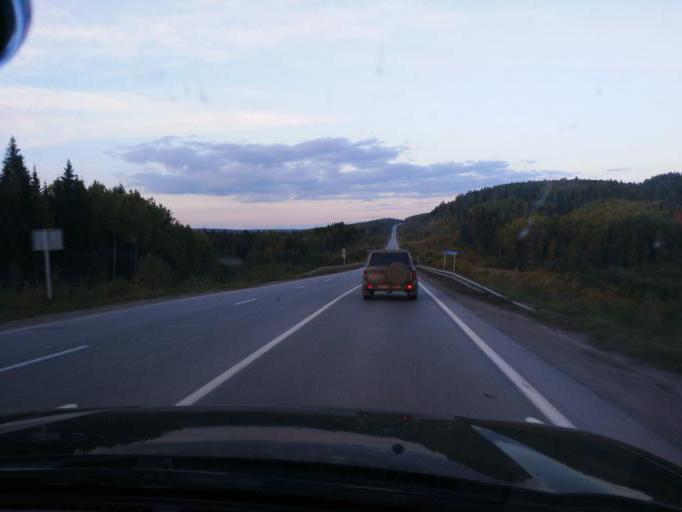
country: RU
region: Perm
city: Polazna
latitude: 58.2903
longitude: 56.5103
